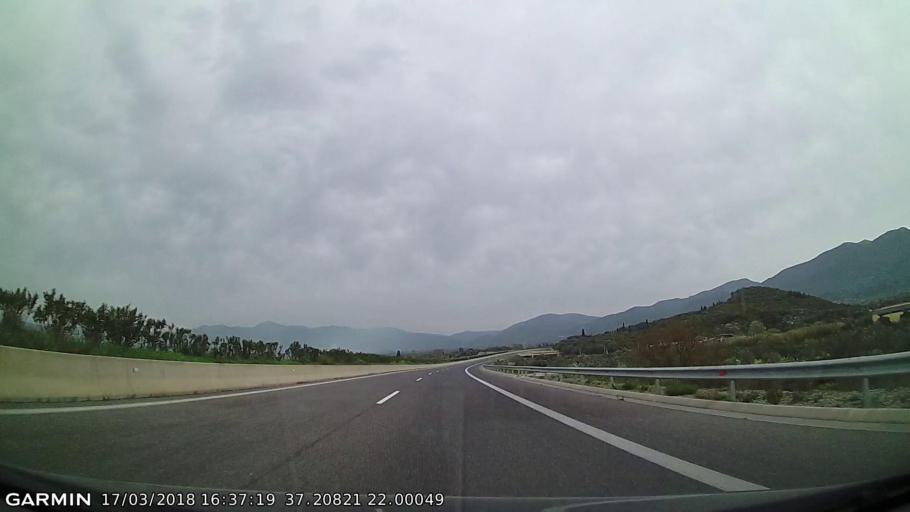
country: GR
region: Peloponnese
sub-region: Nomos Messinias
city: Meligalas
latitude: 37.2095
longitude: 22.0005
